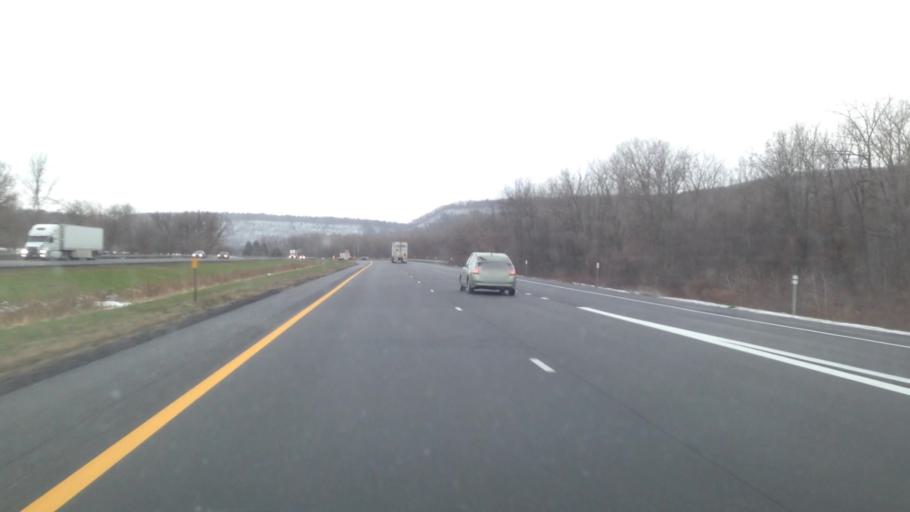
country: US
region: New York
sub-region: Montgomery County
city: Fonda
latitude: 42.9132
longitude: -74.4483
